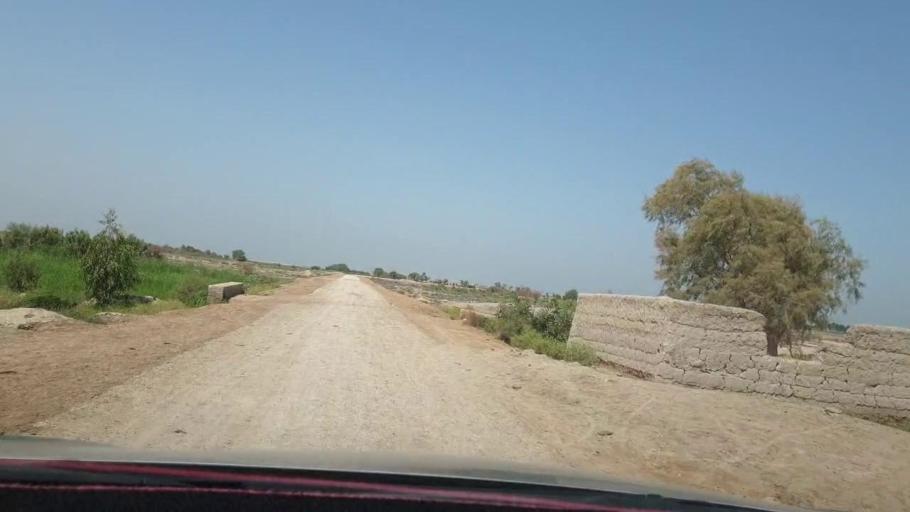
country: PK
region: Sindh
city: Warah
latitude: 27.5202
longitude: 67.7086
